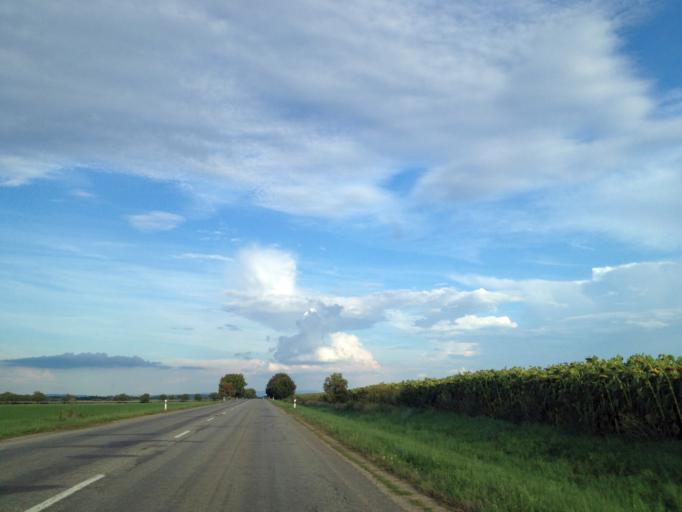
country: SK
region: Nitriansky
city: Svodin
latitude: 47.8892
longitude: 18.4075
